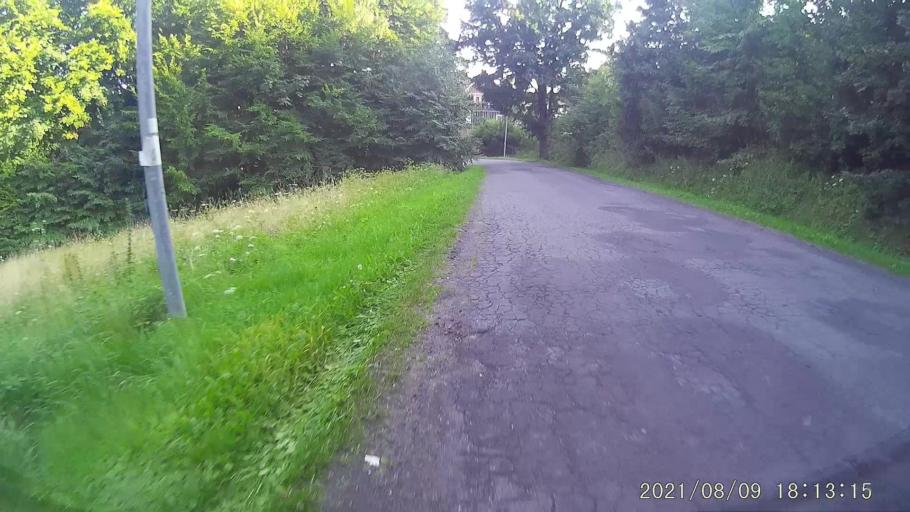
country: PL
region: Lower Silesian Voivodeship
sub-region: Powiat klodzki
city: Klodzko
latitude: 50.4918
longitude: 16.6641
